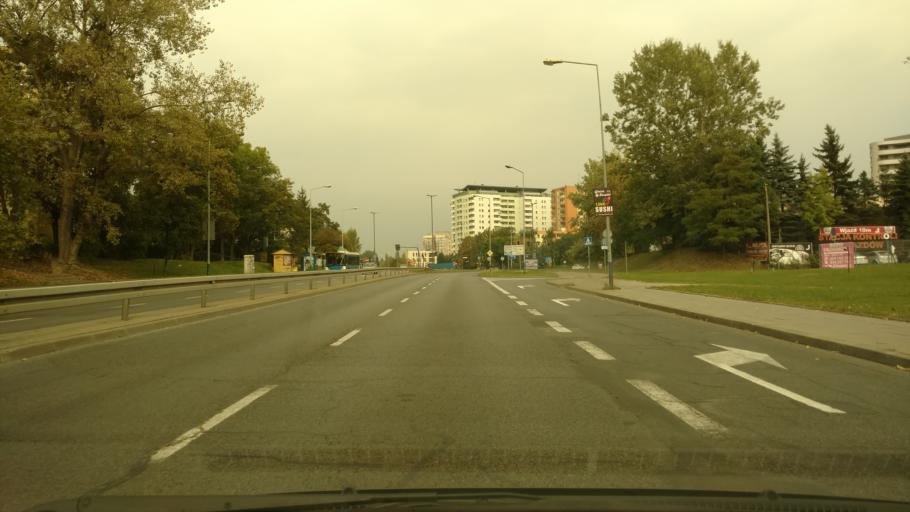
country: PL
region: Lesser Poland Voivodeship
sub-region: Krakow
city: Krakow
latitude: 50.0874
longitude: 19.9728
